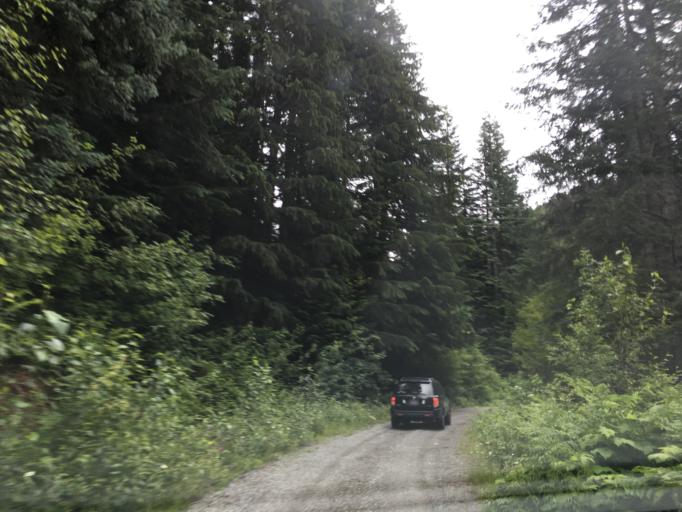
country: US
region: Washington
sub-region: Chelan County
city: Leavenworth
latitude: 47.7495
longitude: -121.1226
